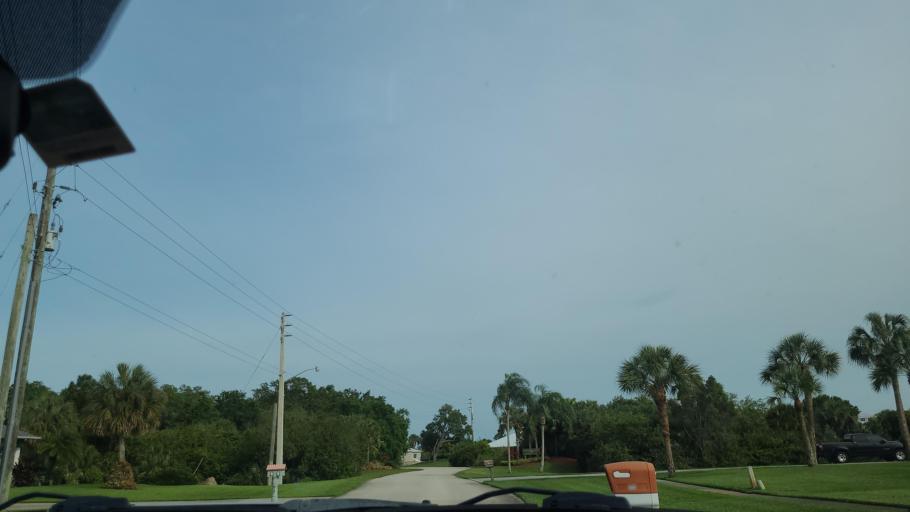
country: US
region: Florida
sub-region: Indian River County
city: Sebastian
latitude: 27.7892
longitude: -80.4792
